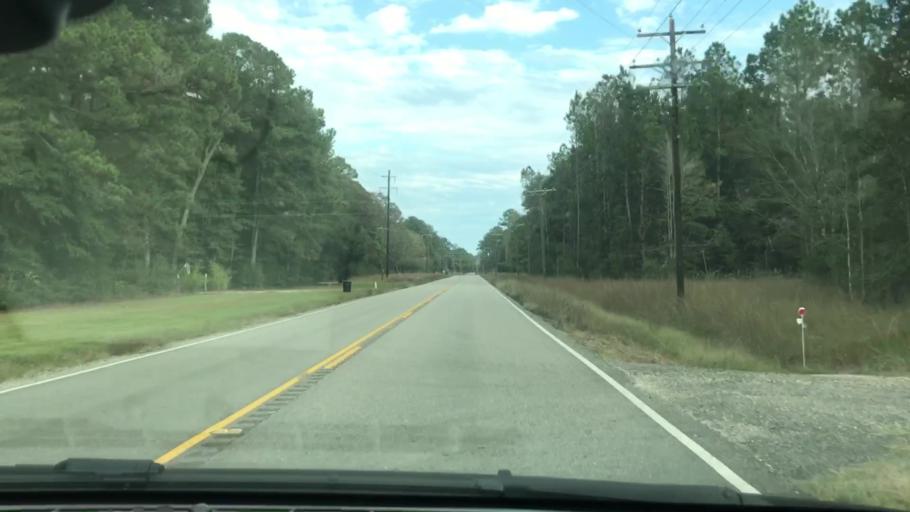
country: US
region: Louisiana
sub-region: Saint Tammany Parish
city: Abita Springs
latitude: 30.5347
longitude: -89.8965
